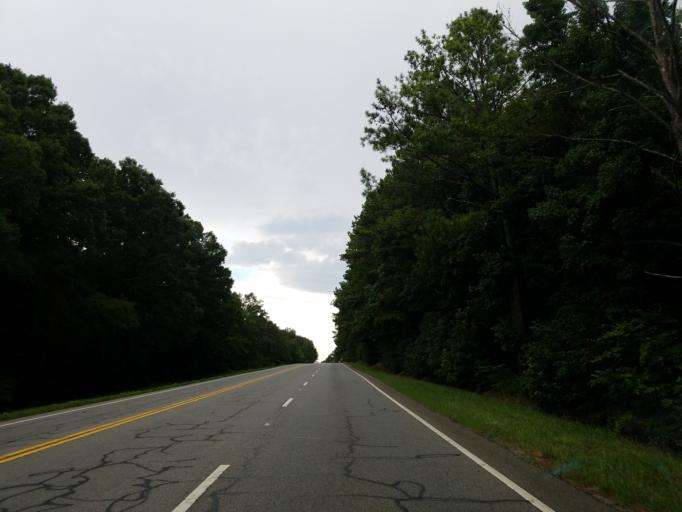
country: US
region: Georgia
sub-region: Bartow County
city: Adairsville
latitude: 34.2917
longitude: -84.8751
